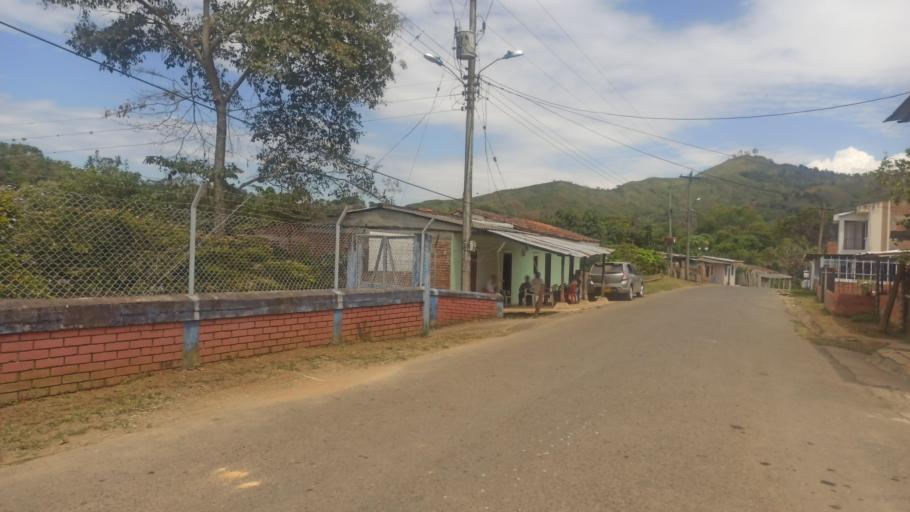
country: CO
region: Valle del Cauca
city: Jamundi
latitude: 3.1878
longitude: -76.6320
